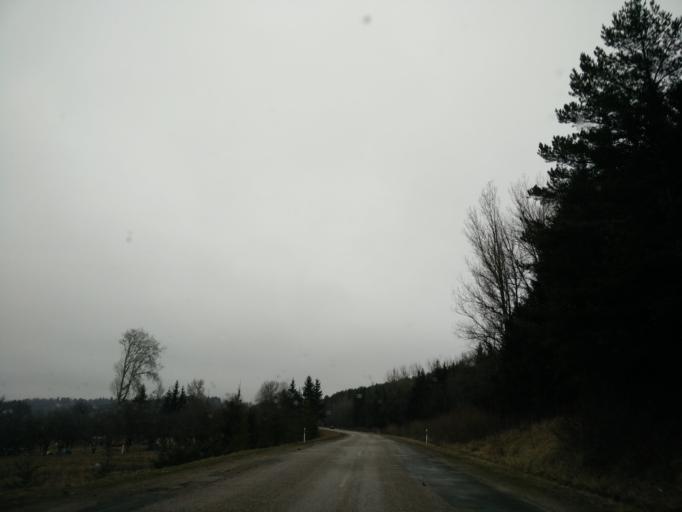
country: LT
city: Ariogala
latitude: 55.2915
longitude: 23.4430
